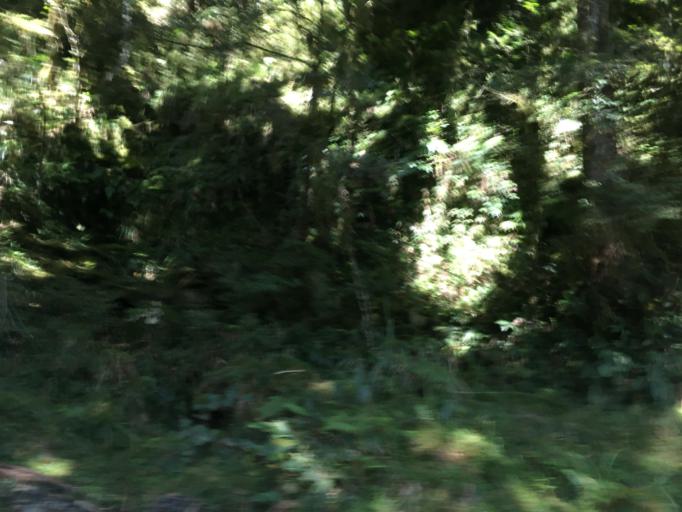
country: TW
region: Taiwan
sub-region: Yilan
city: Yilan
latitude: 24.6170
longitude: 121.4666
